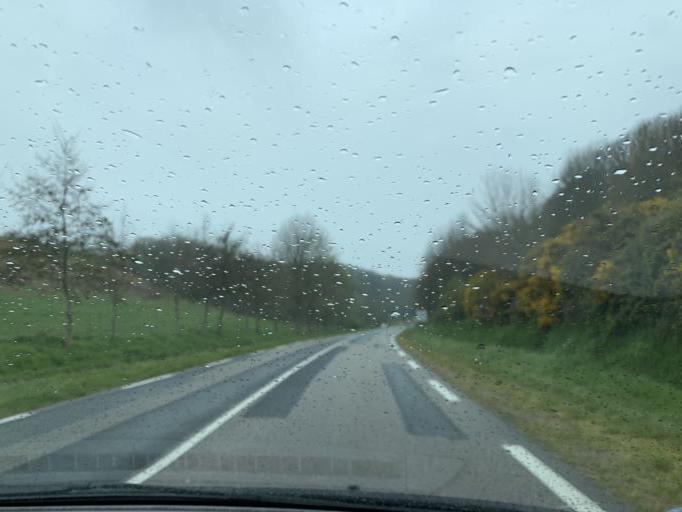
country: FR
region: Haute-Normandie
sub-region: Departement de la Seine-Maritime
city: Etretat
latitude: 49.6984
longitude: 0.2021
